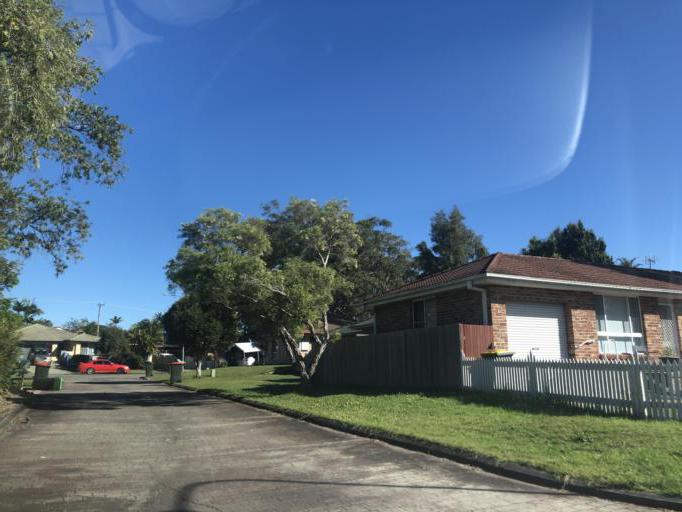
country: AU
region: New South Wales
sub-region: Coffs Harbour
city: Toormina
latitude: -30.3700
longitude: 153.0850
